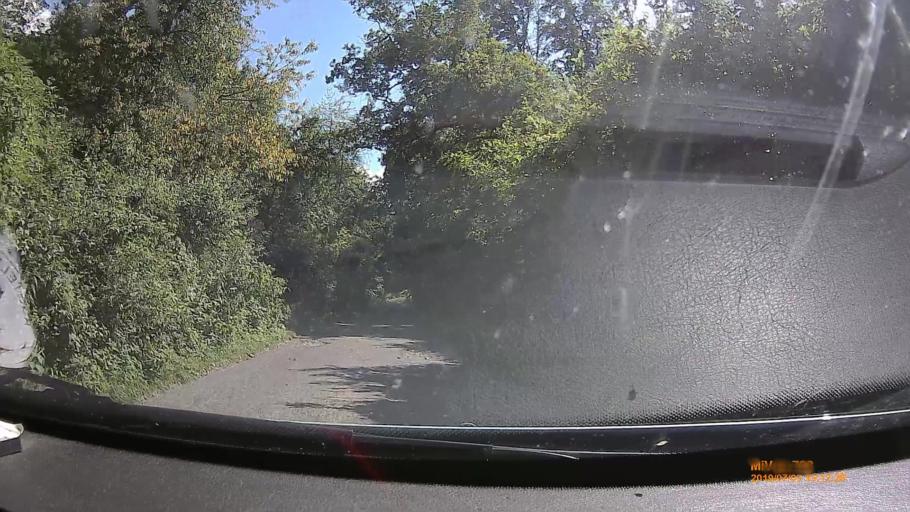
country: HU
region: Borsod-Abauj-Zemplen
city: Farkaslyuk
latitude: 48.2180
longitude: 20.3729
